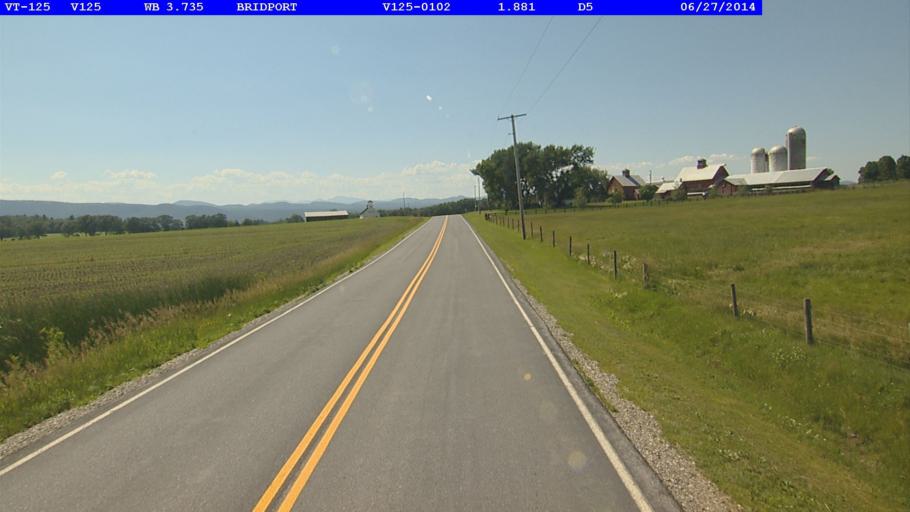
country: US
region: New York
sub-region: Essex County
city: Port Henry
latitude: 44.0034
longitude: -73.3709
